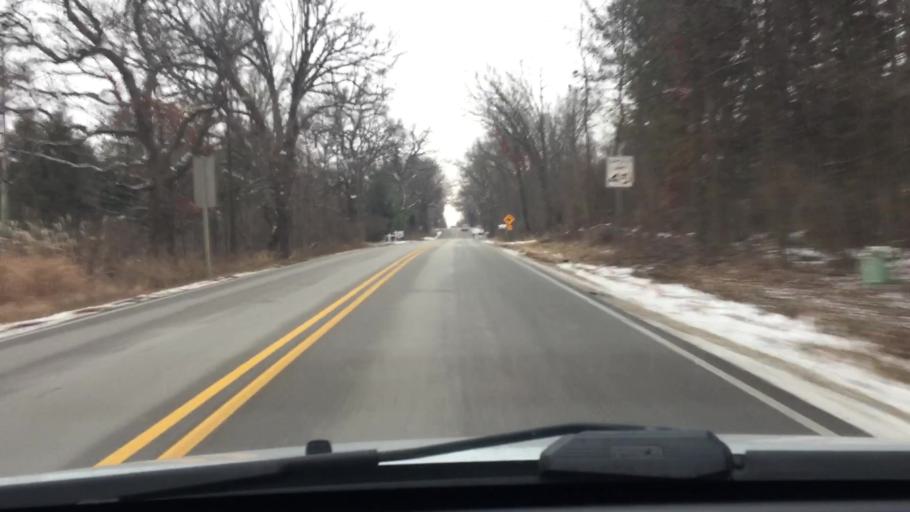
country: US
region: Wisconsin
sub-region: Waukesha County
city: Delafield
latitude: 43.0311
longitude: -88.4042
